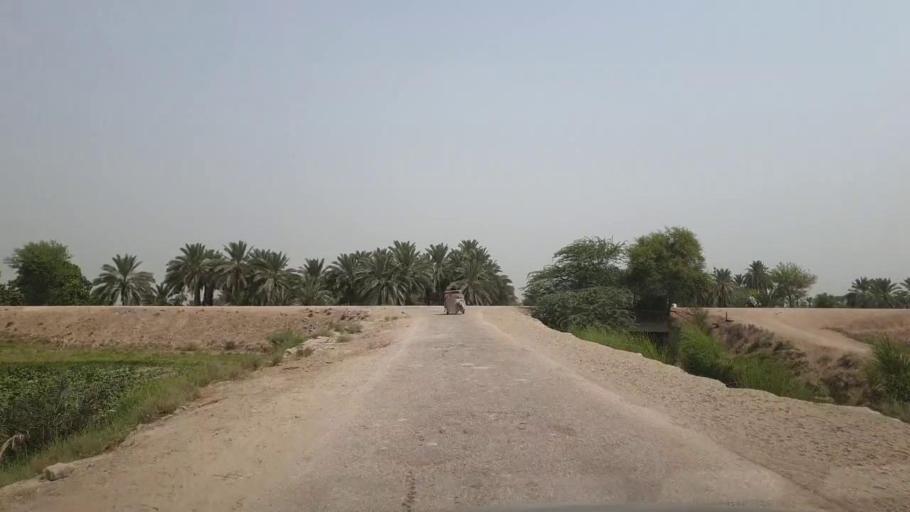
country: PK
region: Sindh
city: Gambat
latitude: 27.4372
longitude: 68.5592
